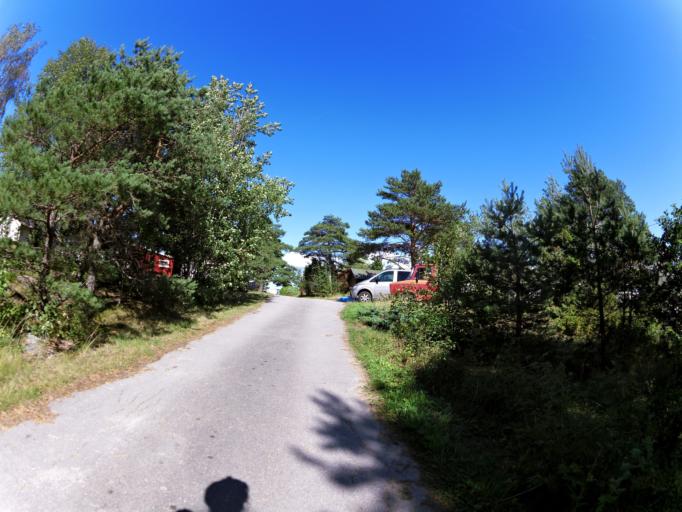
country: NO
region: Ostfold
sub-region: Fredrikstad
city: Fredrikstad
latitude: 59.1734
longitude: 10.8556
